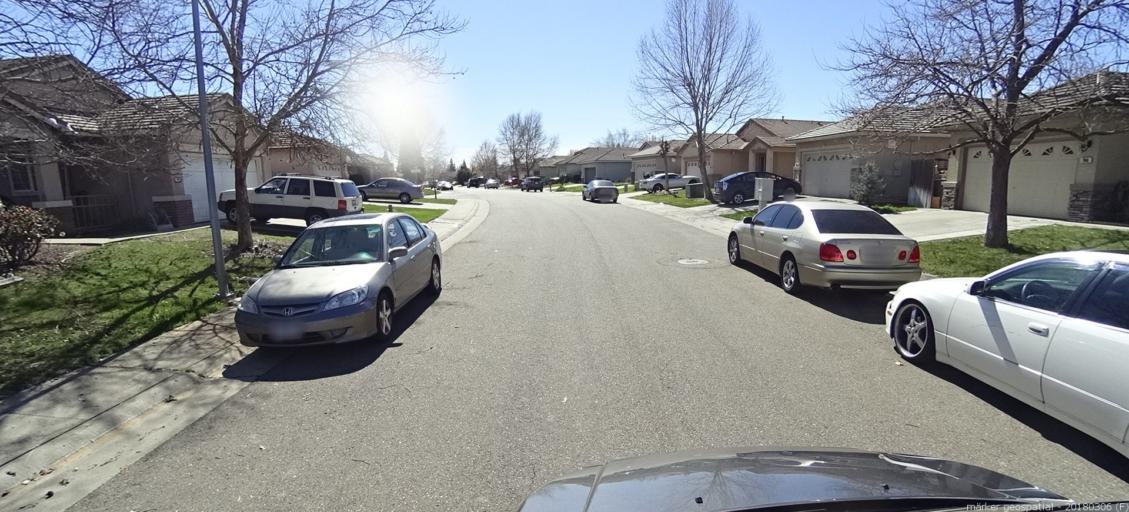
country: US
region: California
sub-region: Sacramento County
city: Vineyard
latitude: 38.4719
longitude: -121.3551
